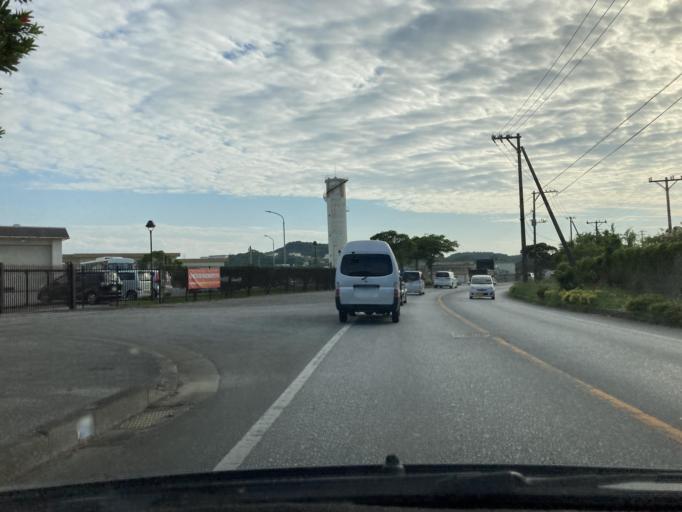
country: JP
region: Okinawa
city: Okinawa
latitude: 26.3653
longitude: 127.7975
